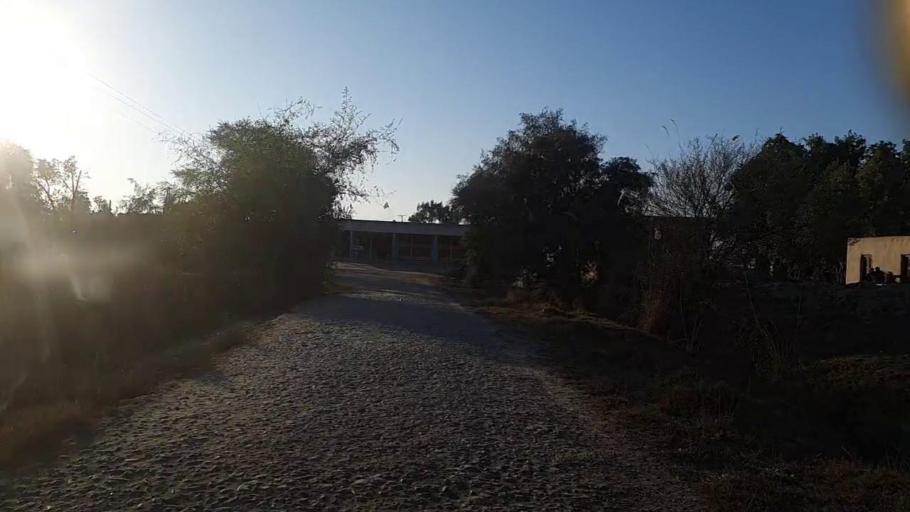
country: PK
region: Sindh
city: Khairpur
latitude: 27.8969
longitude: 69.6934
